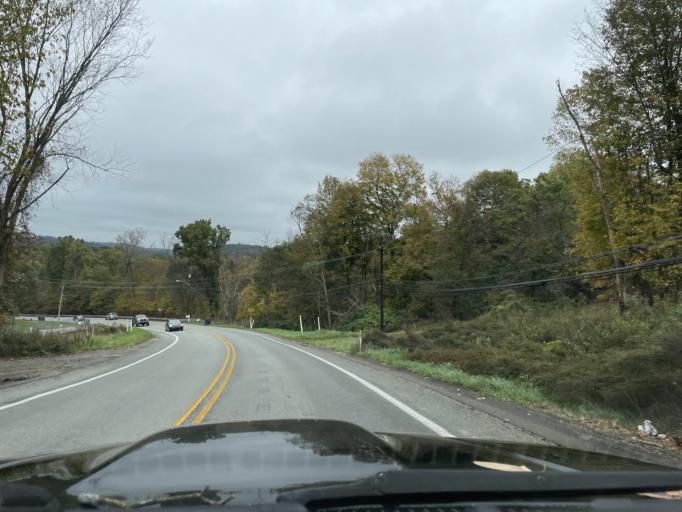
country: US
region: Pennsylvania
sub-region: Allegheny County
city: Springdale
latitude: 40.5345
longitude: -79.7656
